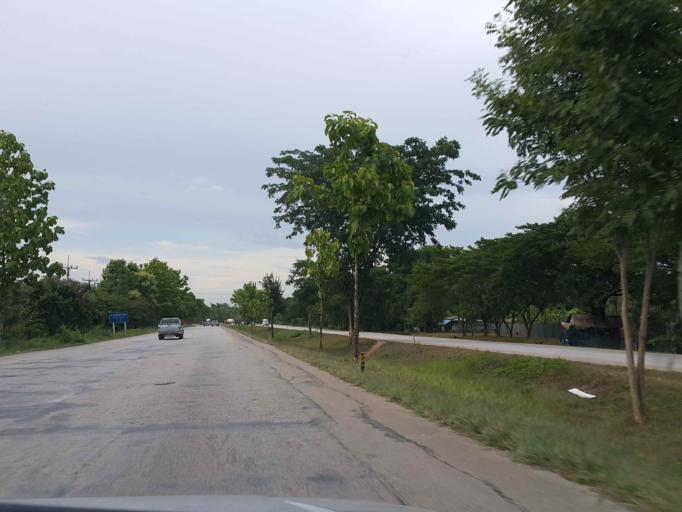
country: TH
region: Lampang
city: Ko Kha
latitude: 18.1761
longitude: 99.4081
